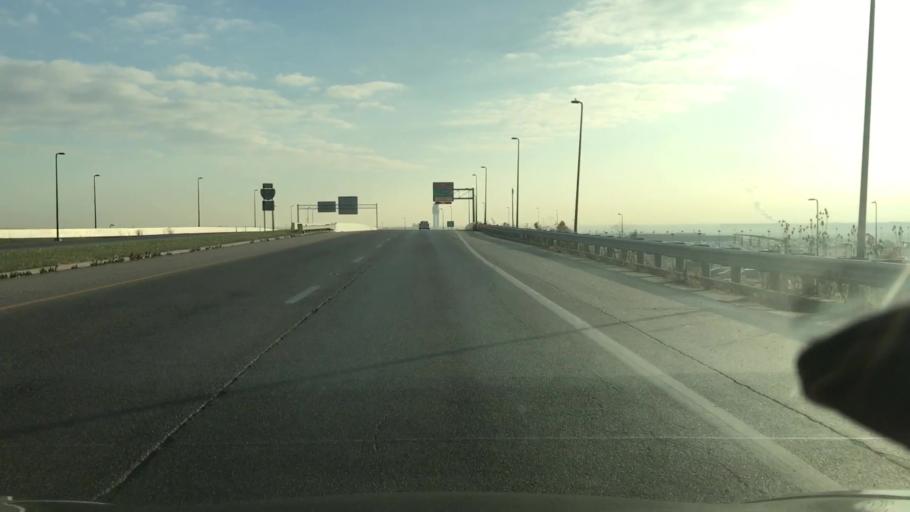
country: US
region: Ohio
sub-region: Franklin County
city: Bexley
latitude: 39.9996
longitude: -82.9144
